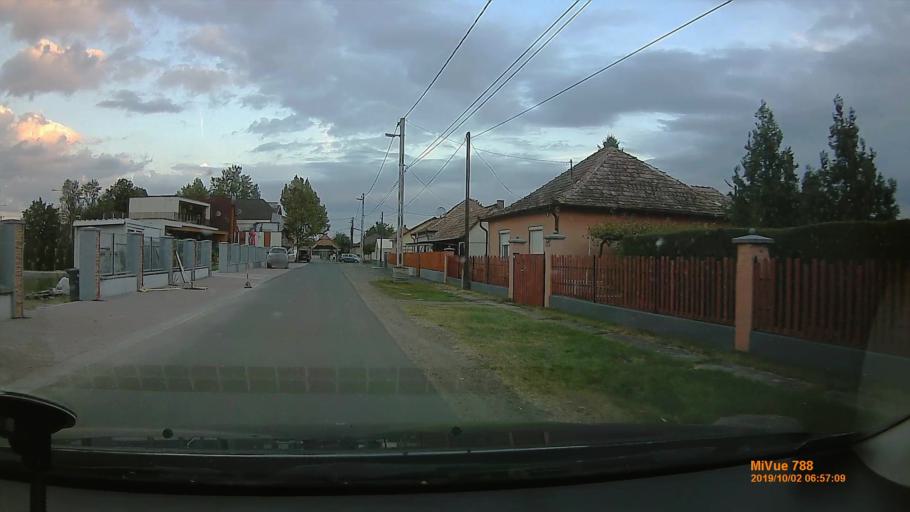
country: HU
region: Heves
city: Zagyvaszanto
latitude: 47.7667
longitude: 19.6644
